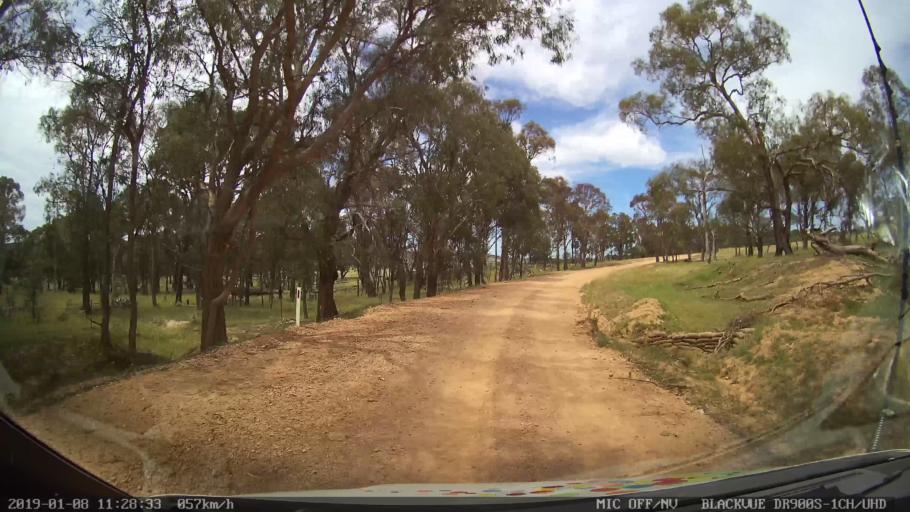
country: AU
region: New South Wales
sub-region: Guyra
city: Guyra
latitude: -30.2971
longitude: 151.5546
